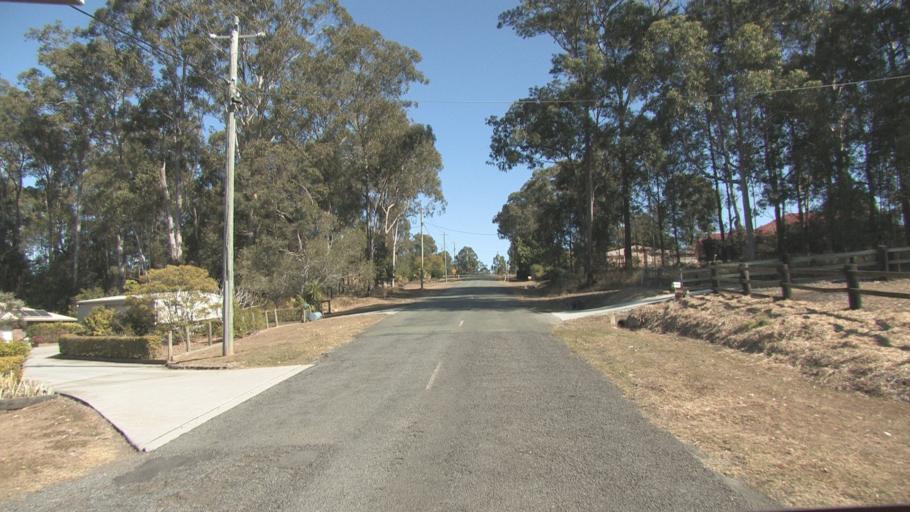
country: AU
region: Queensland
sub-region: Logan
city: Cedar Vale
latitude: -27.8797
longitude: 153.0089
